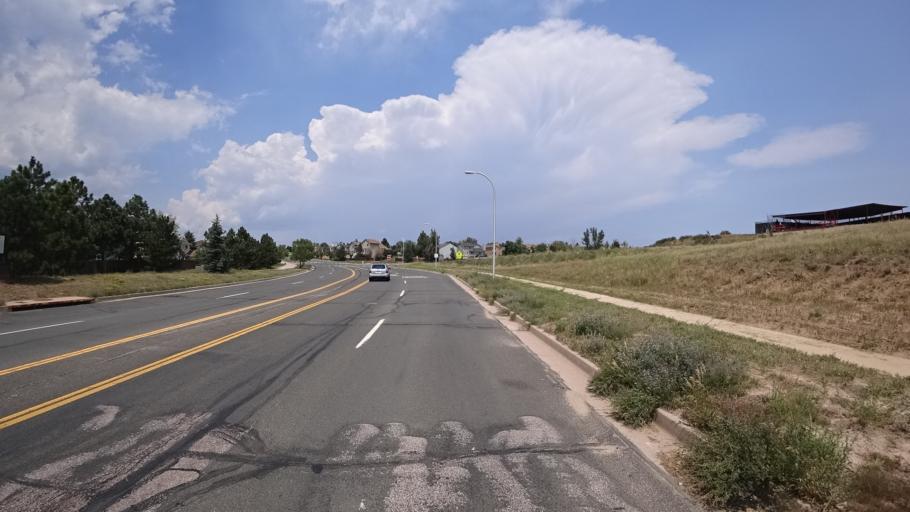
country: US
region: Colorado
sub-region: El Paso County
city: Black Forest
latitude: 38.9557
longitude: -104.7391
